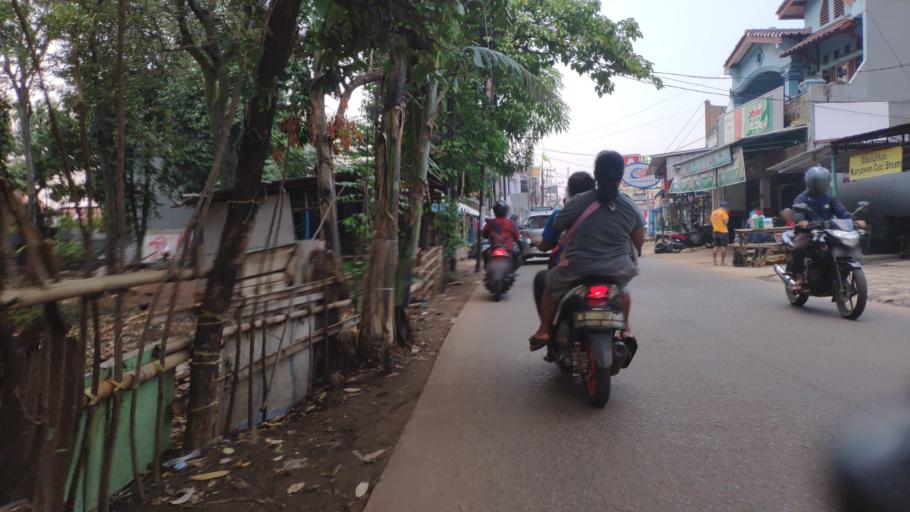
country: ID
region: West Java
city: Pamulang
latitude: -6.3288
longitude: 106.7971
